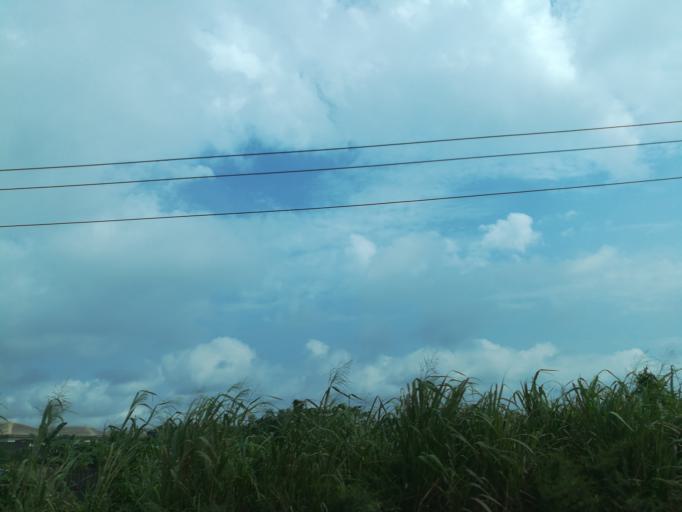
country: NG
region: Lagos
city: Ikorodu
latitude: 6.6634
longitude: 3.5987
